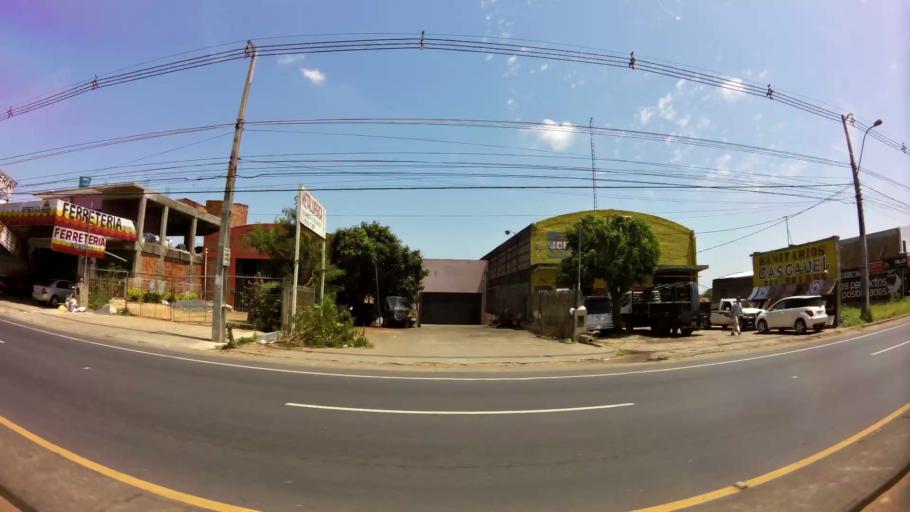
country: PY
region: Central
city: Nemby
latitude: -25.3742
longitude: -57.5571
